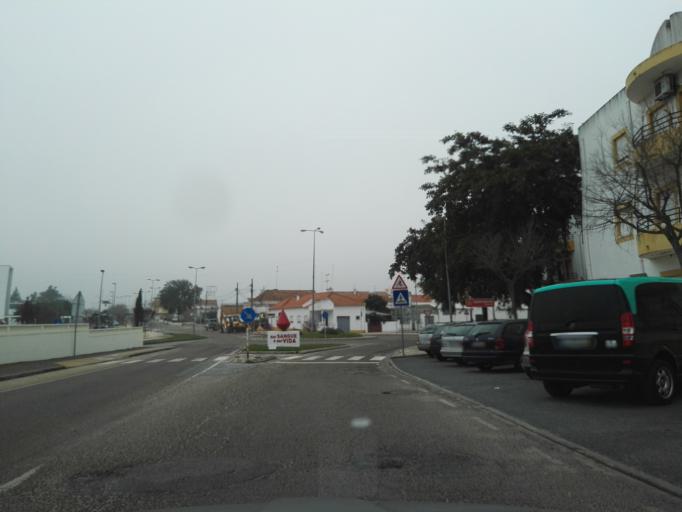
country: PT
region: Evora
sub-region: Vendas Novas
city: Vendas Novas
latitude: 38.6746
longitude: -8.4563
